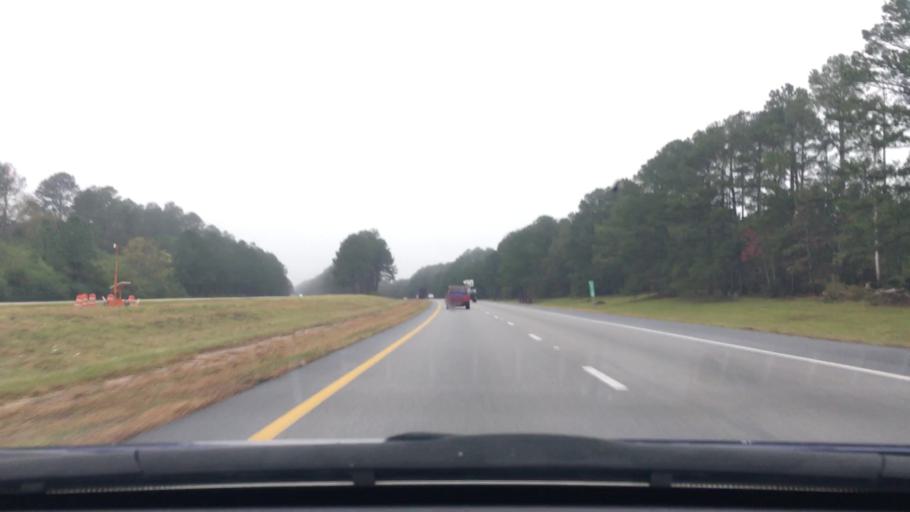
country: US
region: South Carolina
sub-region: Lee County
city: Bishopville
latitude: 34.2009
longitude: -80.3486
